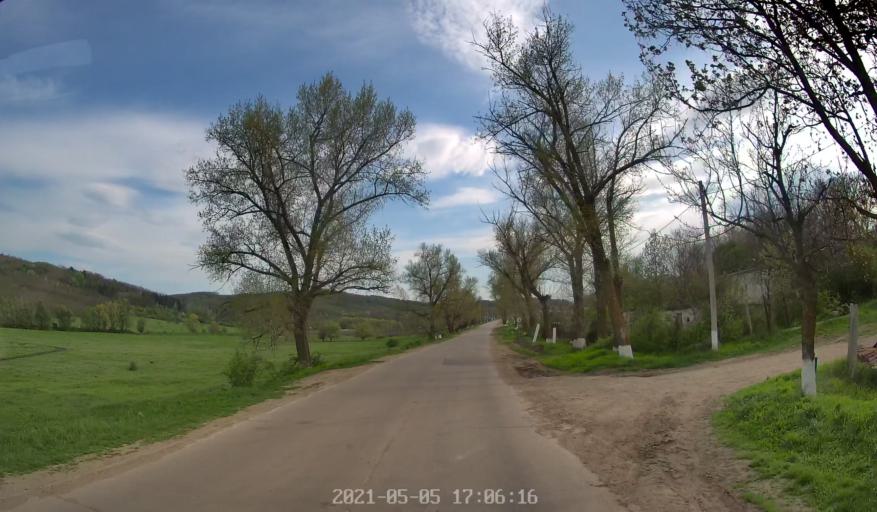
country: MD
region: Chisinau
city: Vadul lui Voda
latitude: 47.0218
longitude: 29.1401
